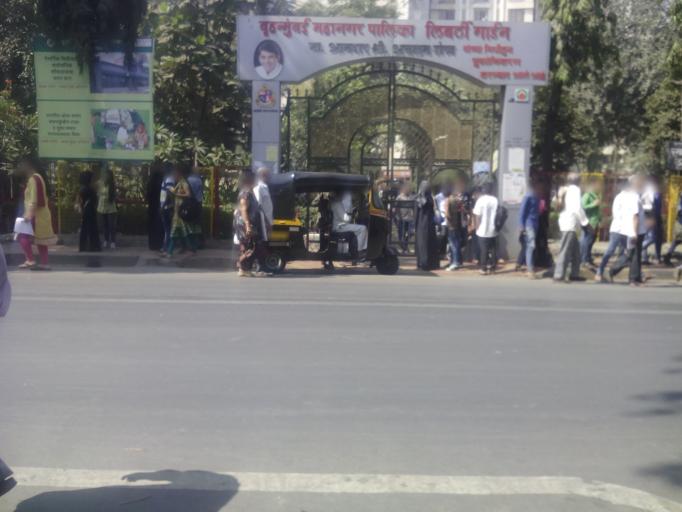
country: IN
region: Maharashtra
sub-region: Mumbai Suburban
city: Borivli
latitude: 19.1873
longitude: 72.8416
